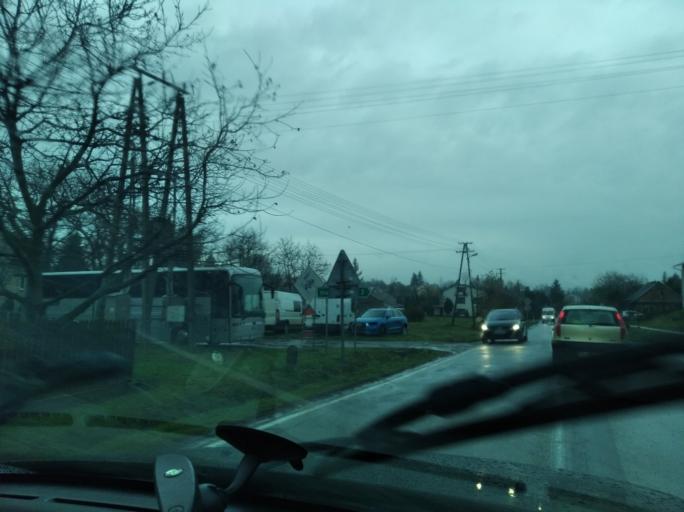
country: PL
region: Subcarpathian Voivodeship
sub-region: Powiat lancucki
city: Albigowa
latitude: 50.0130
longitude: 22.2234
